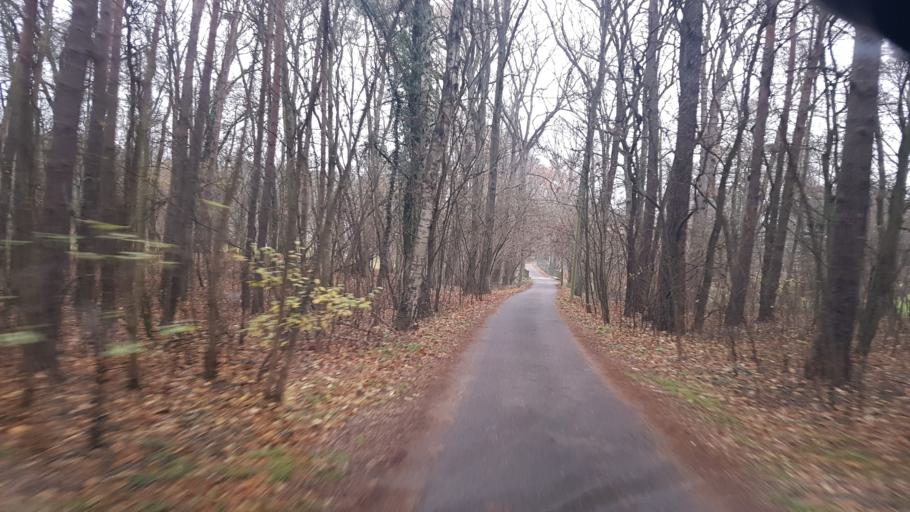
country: DE
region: Brandenburg
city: Schenkendobern
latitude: 51.9714
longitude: 14.6501
